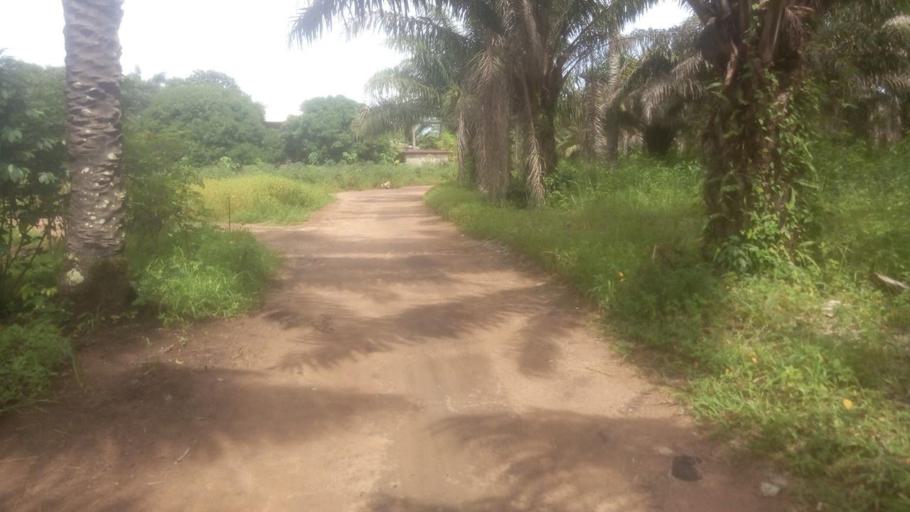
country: SL
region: Northern Province
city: Masoyila
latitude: 8.5907
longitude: -13.1893
